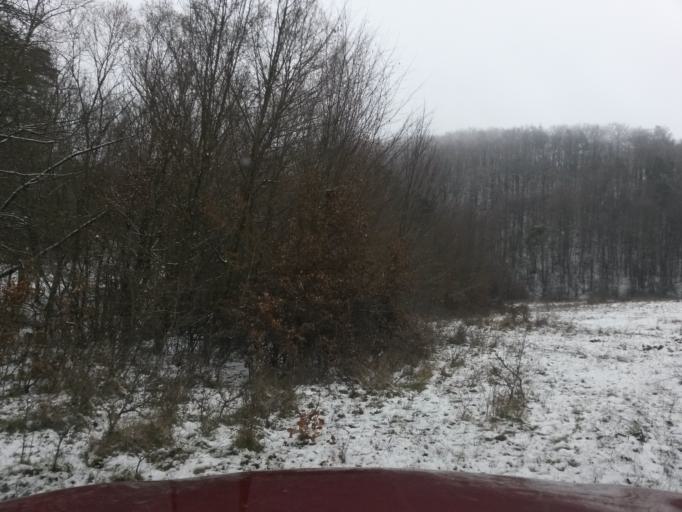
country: SK
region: Presovsky
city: Sabinov
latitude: 48.9713
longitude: 21.0887
